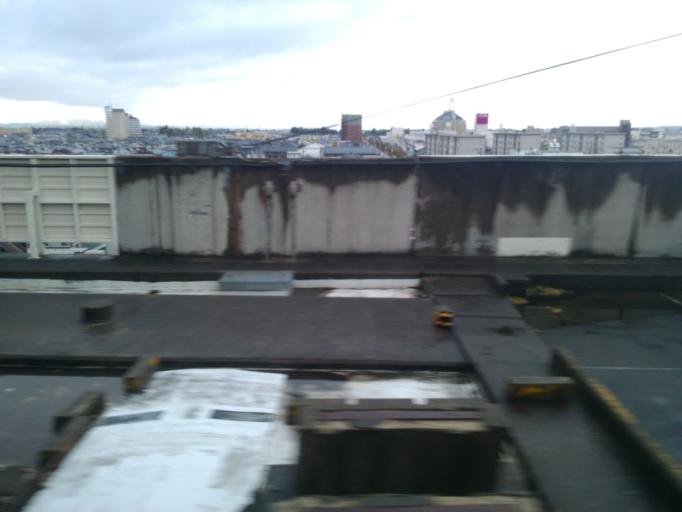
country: JP
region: Miyagi
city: Furukawa
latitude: 38.5692
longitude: 140.9672
